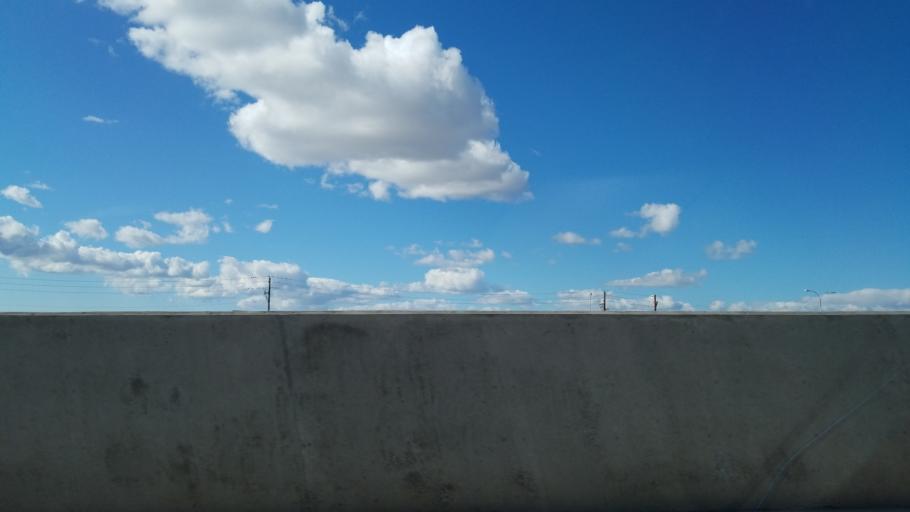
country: US
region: Arizona
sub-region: Maricopa County
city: Tolleson
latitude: 33.4417
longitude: -112.1878
